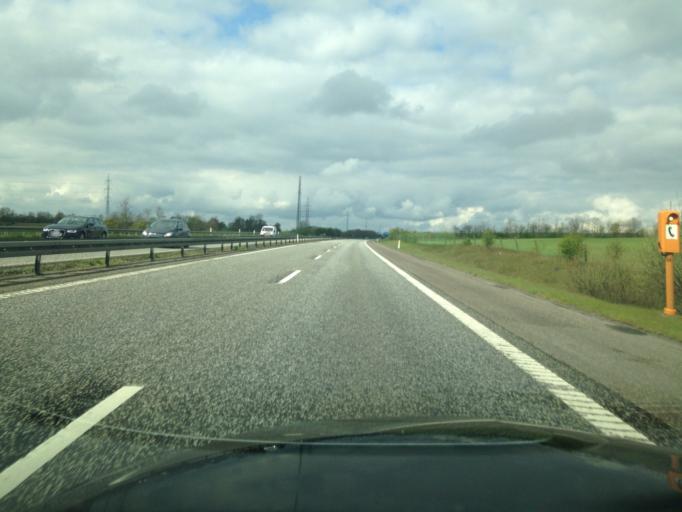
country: DK
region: South Denmark
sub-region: Kolding Kommune
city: Lunderskov
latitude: 55.5077
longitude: 9.3380
